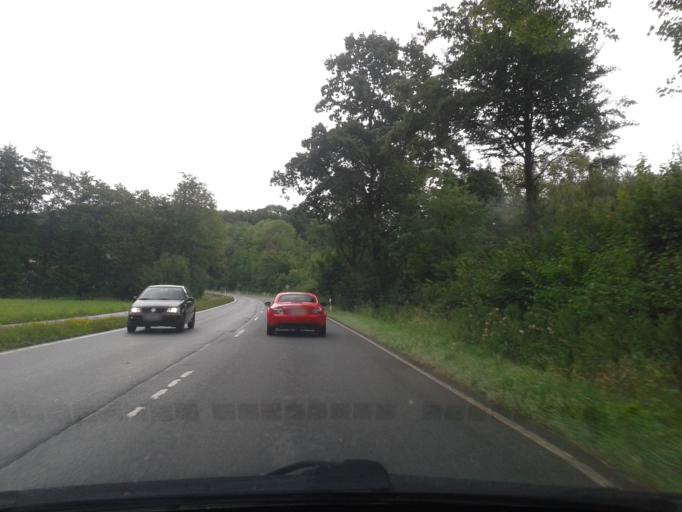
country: DE
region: North Rhine-Westphalia
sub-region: Regierungsbezirk Detmold
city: Horn-Bad Meinberg
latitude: 51.8941
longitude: 8.9457
